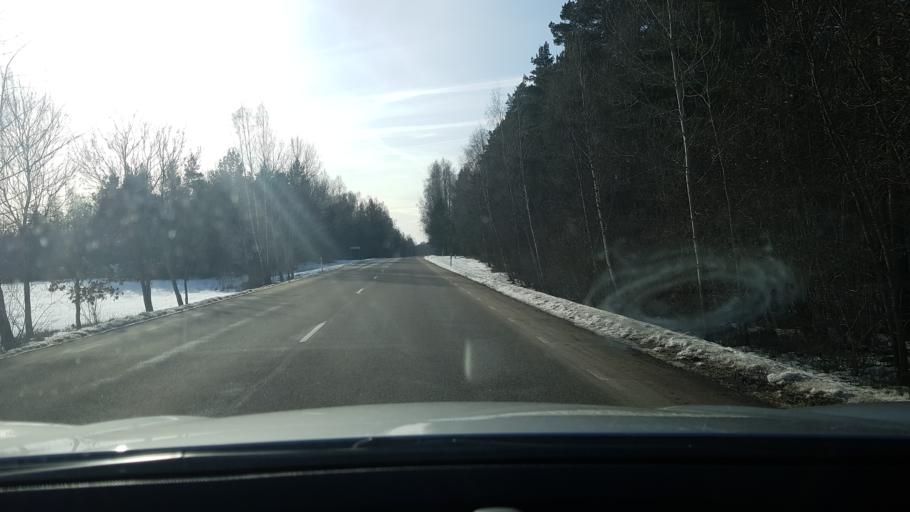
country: EE
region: Saare
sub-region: Orissaare vald
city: Orissaare
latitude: 58.5467
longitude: 23.0575
